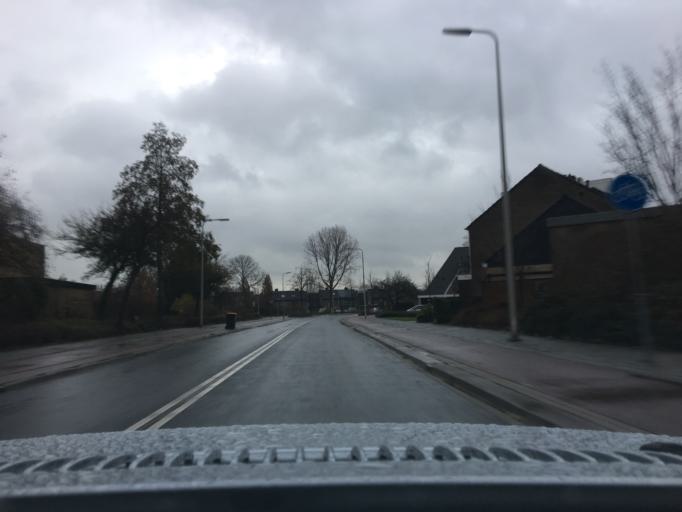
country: NL
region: South Holland
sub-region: Gemeente Hendrik-Ido-Ambacht
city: Hendrik-Ido-Ambacht
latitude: 51.8281
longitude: 4.6512
